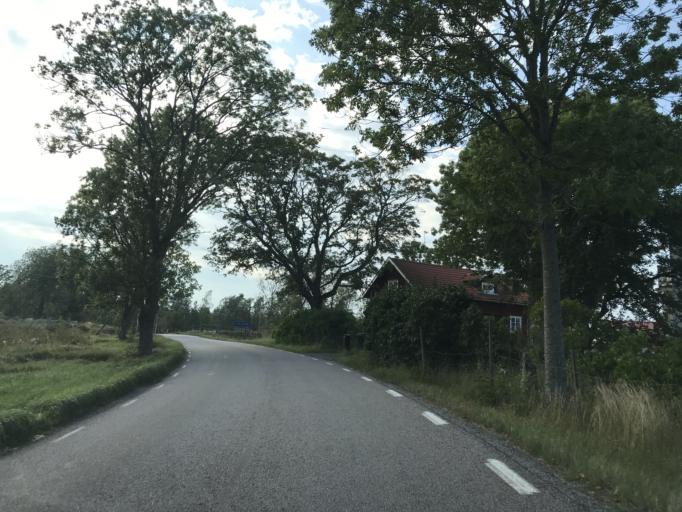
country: SE
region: Stockholm
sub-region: Norrtalje Kommun
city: Bjorko
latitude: 59.8798
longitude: 18.9998
